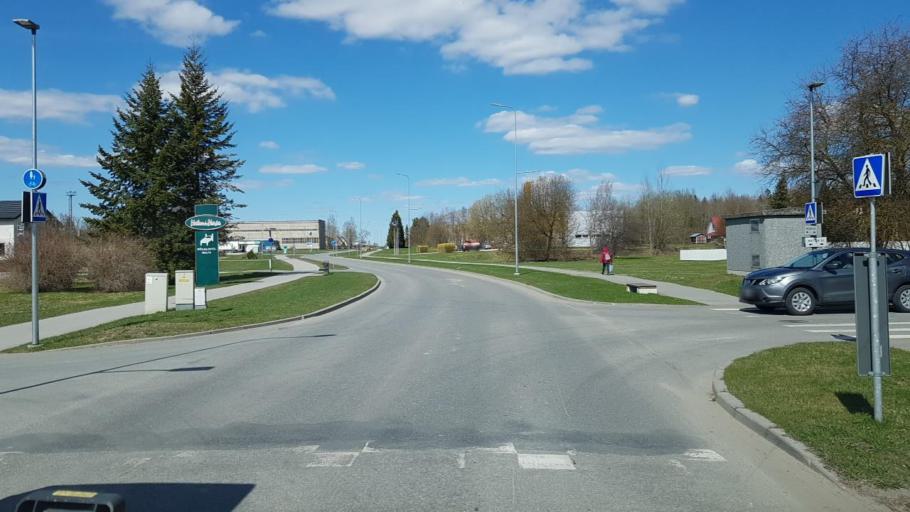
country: EE
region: Jogevamaa
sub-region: Poltsamaa linn
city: Poltsamaa
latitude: 58.6618
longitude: 25.9715
